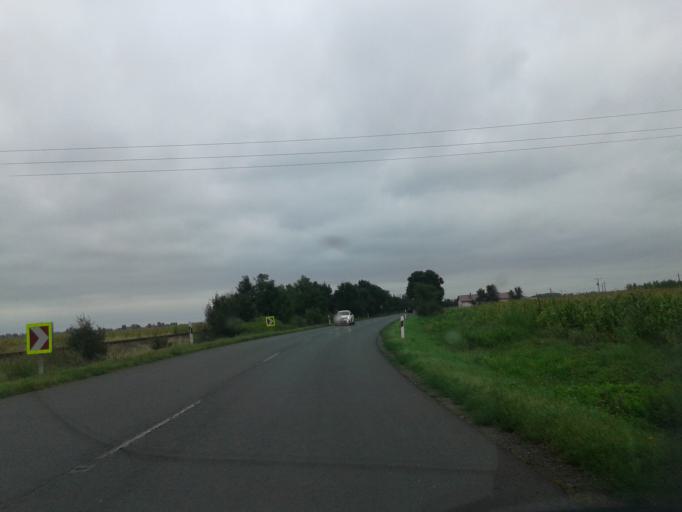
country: HU
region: Bacs-Kiskun
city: Solt
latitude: 46.8429
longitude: 19.0054
